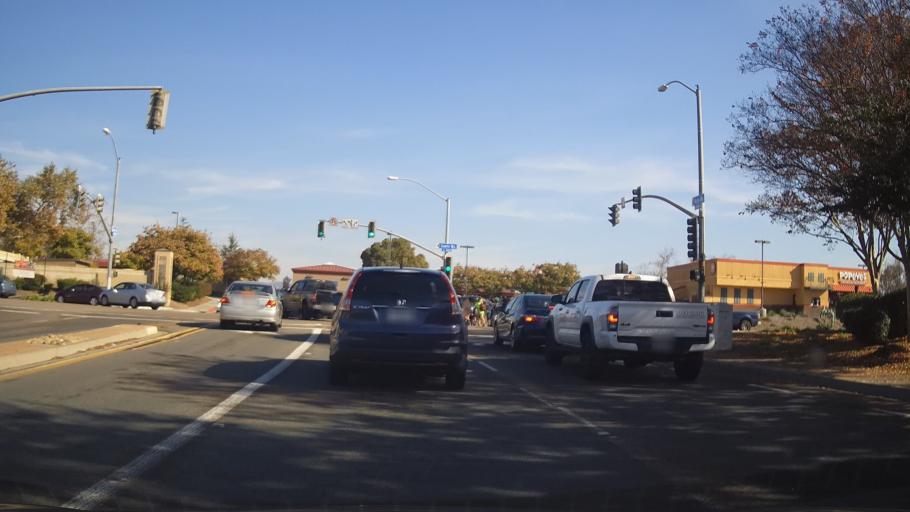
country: US
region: California
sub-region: San Diego County
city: La Mesa
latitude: 32.8093
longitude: -117.1053
